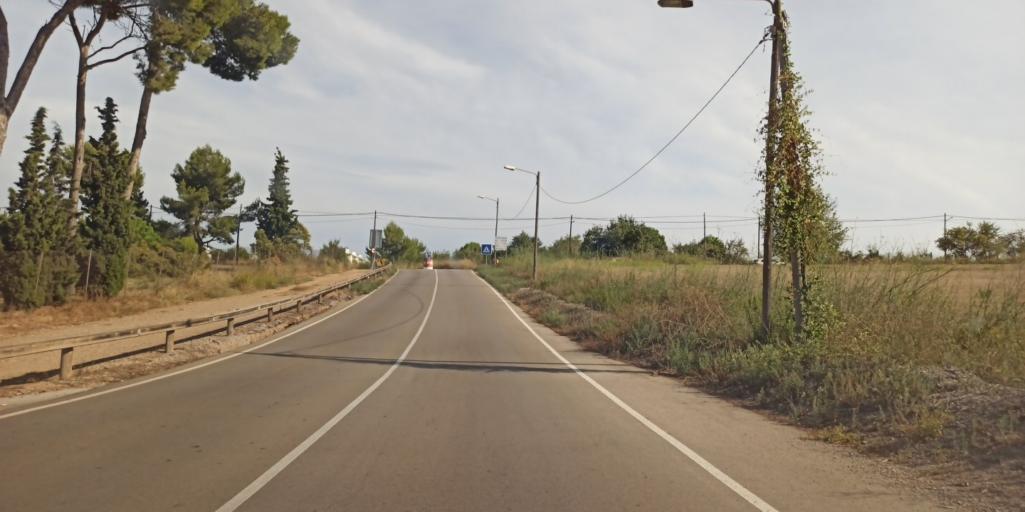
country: ES
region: Catalonia
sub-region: Provincia de Barcelona
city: Santa Coloma de Cervello
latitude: 41.3604
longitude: 2.0249
